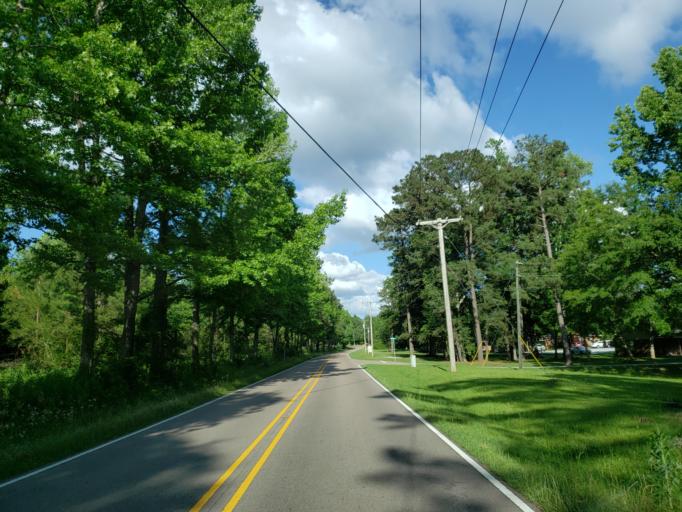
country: US
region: Mississippi
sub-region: Lamar County
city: West Hattiesburg
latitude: 31.2736
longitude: -89.3688
